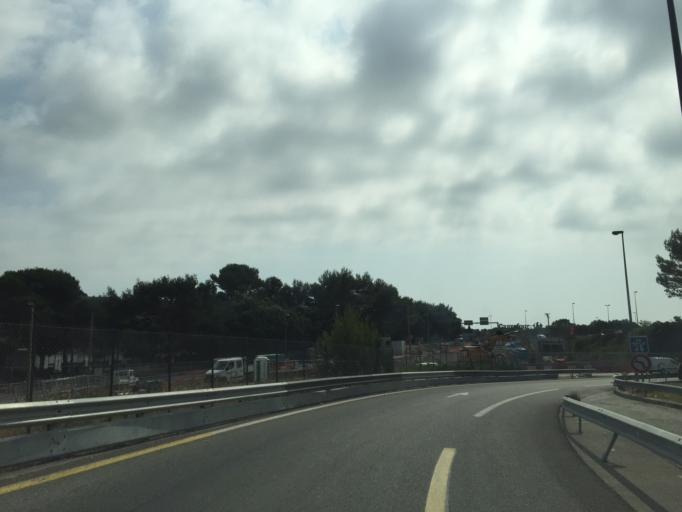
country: FR
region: Provence-Alpes-Cote d'Azur
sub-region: Departement des Alpes-Maritimes
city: Biot
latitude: 43.6040
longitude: 7.0821
